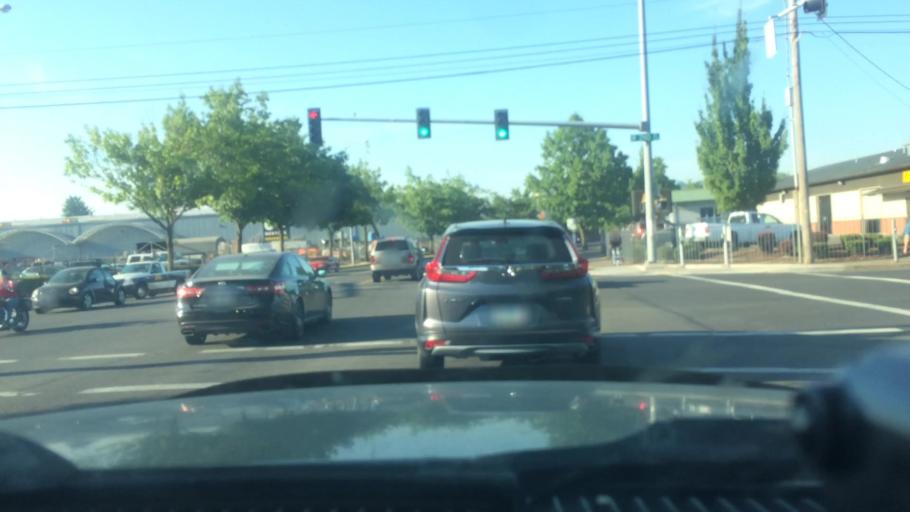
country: US
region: Oregon
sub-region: Lane County
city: Eugene
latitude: 44.0577
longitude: -123.1175
